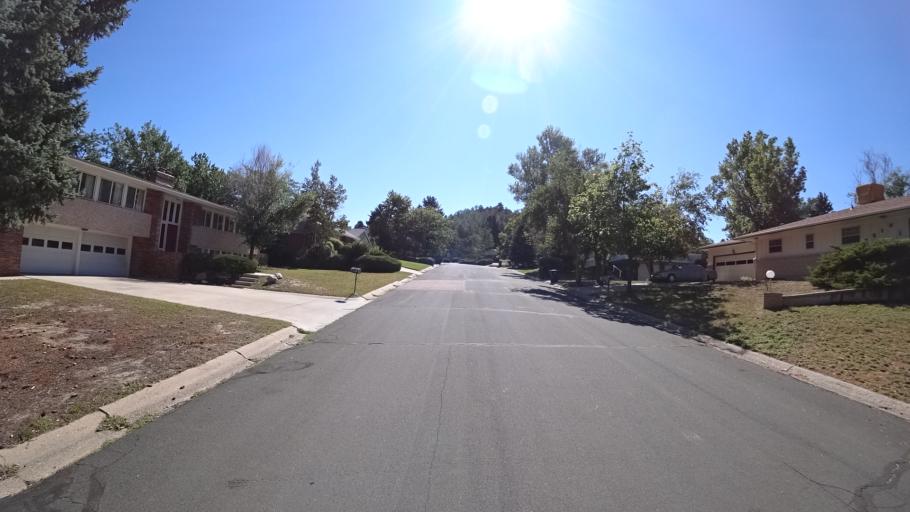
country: US
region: Colorado
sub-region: El Paso County
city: Colorado Springs
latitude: 38.8757
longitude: -104.7805
